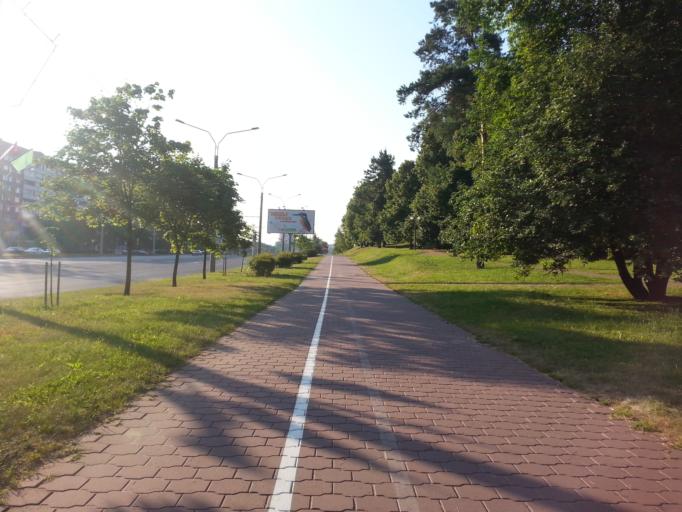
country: BY
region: Minsk
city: Vyaliki Trastsyanets
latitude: 53.8650
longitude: 27.6624
